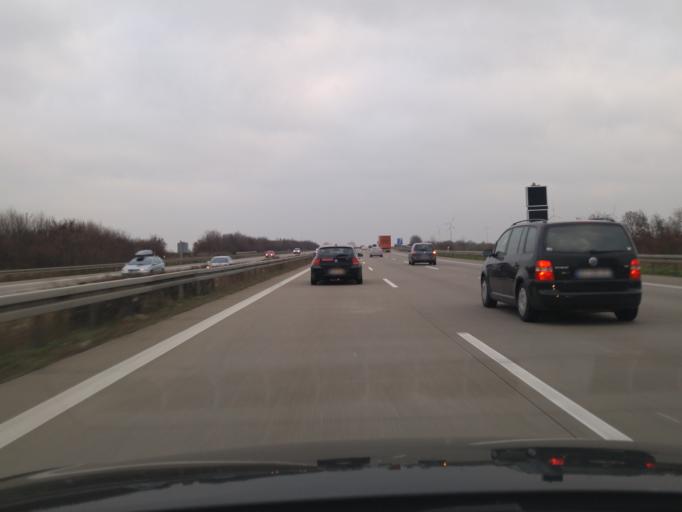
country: DE
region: Saxony-Anhalt
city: Erxleben
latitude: 52.2002
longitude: 11.2363
